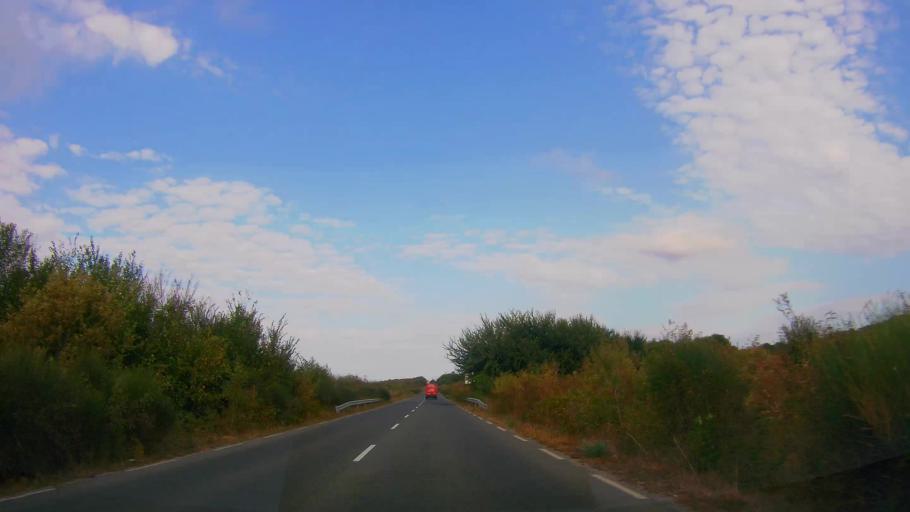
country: BG
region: Burgas
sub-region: Obshtina Sozopol
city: Sozopol
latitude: 42.3652
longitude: 27.6938
